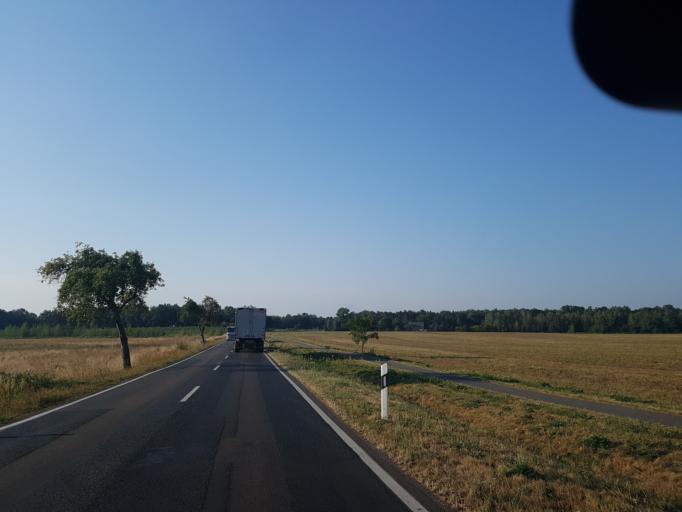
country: DE
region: Brandenburg
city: Hohenleipisch
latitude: 51.4791
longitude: 13.5485
